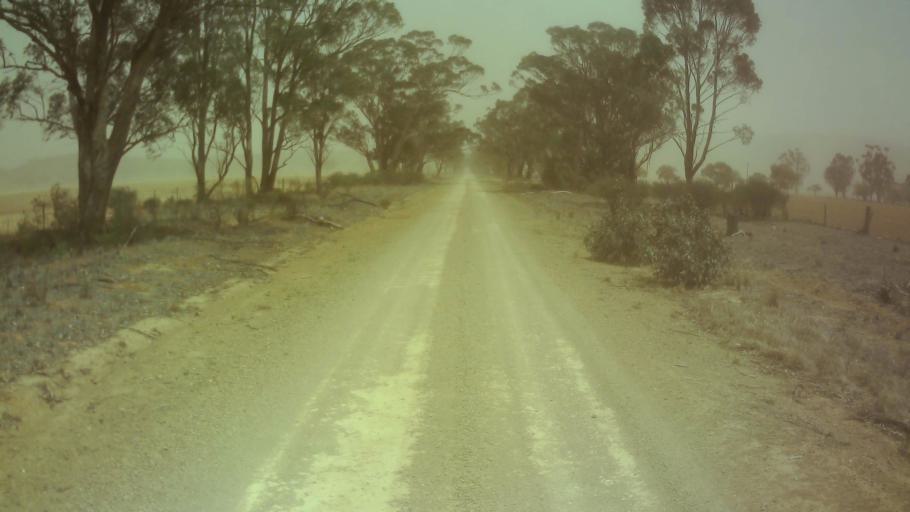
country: AU
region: New South Wales
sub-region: Weddin
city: Grenfell
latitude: -33.7119
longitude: 147.9671
